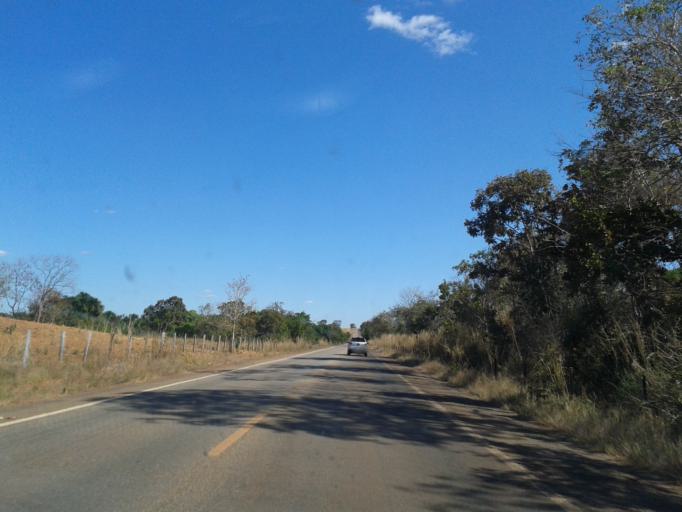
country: BR
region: Goias
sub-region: Crixas
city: Crixas
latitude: -14.1315
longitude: -50.3519
